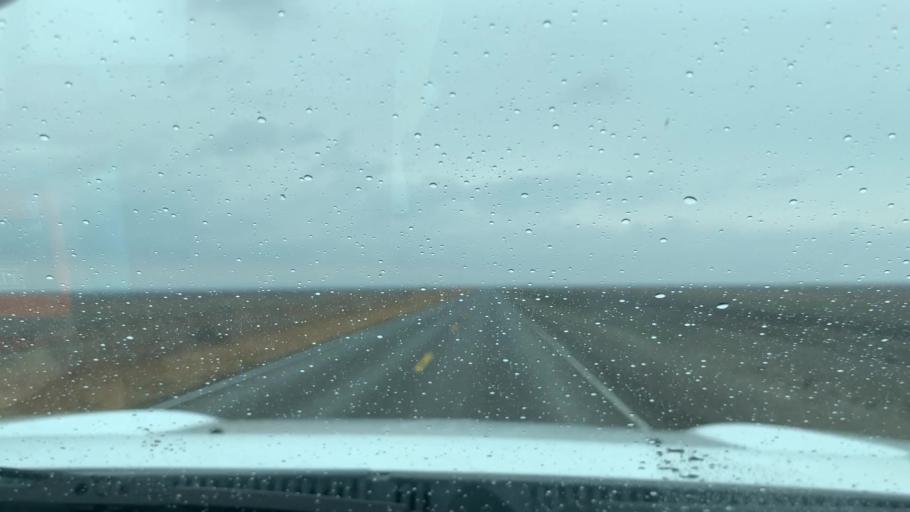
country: US
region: California
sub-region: Kings County
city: Corcoran
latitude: 35.9341
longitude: -119.7241
